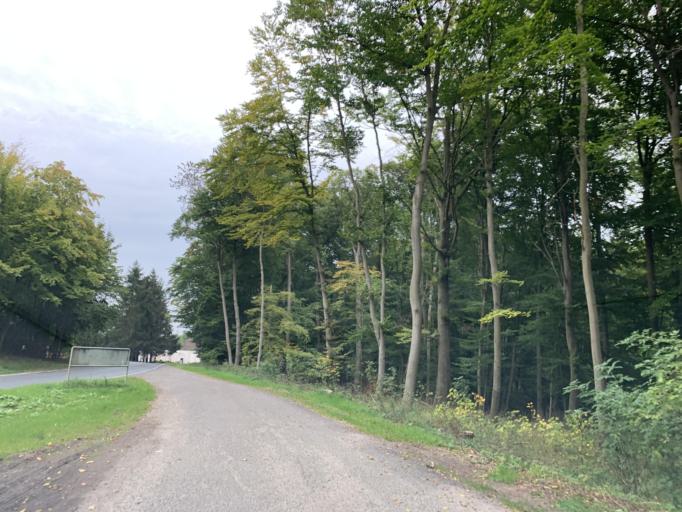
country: DE
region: Mecklenburg-Vorpommern
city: Woldegk
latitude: 53.3355
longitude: 13.6169
